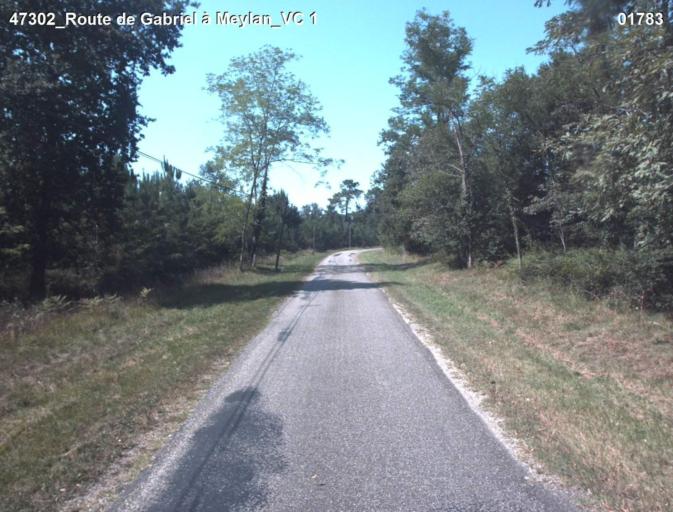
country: FR
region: Aquitaine
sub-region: Departement du Lot-et-Garonne
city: Mezin
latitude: 44.0667
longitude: 0.1389
